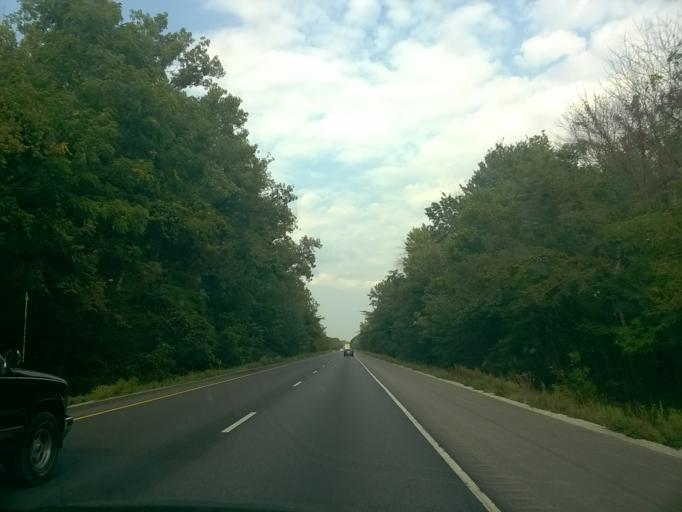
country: US
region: Indiana
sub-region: Clay County
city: Brazil
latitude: 39.4563
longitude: -87.0928
